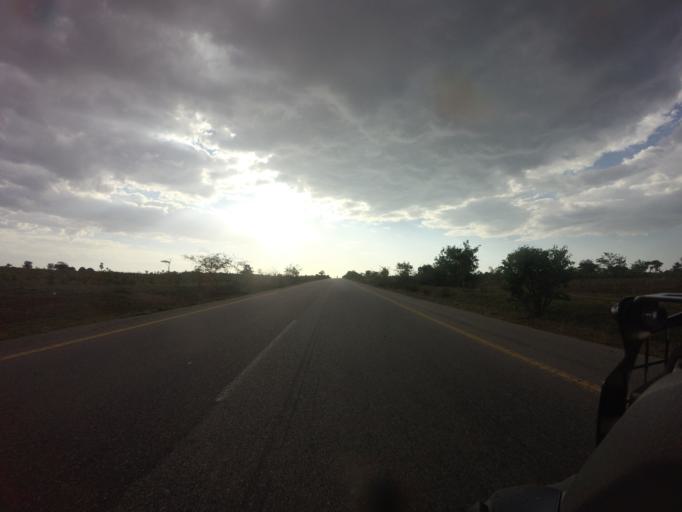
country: AO
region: Huila
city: Lubango
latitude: -14.6049
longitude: 14.0020
